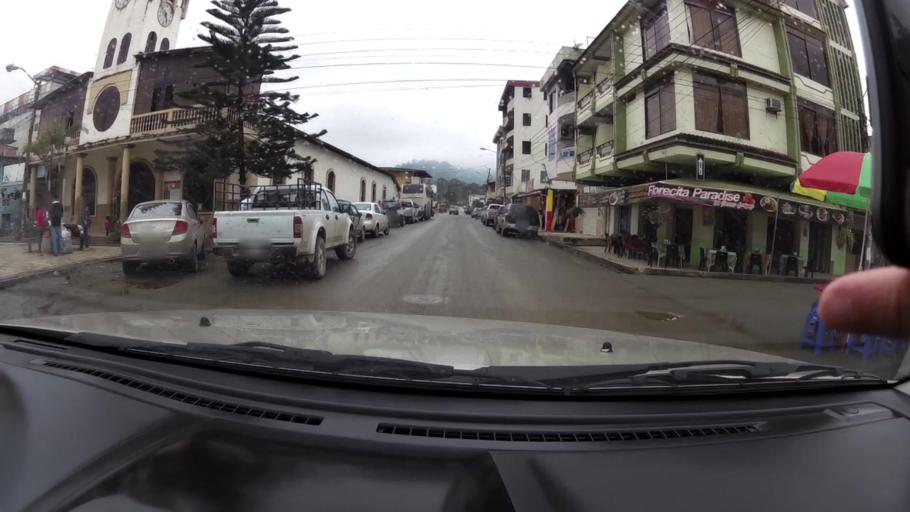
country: EC
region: Guayas
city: Balao
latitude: -3.0619
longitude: -79.7458
